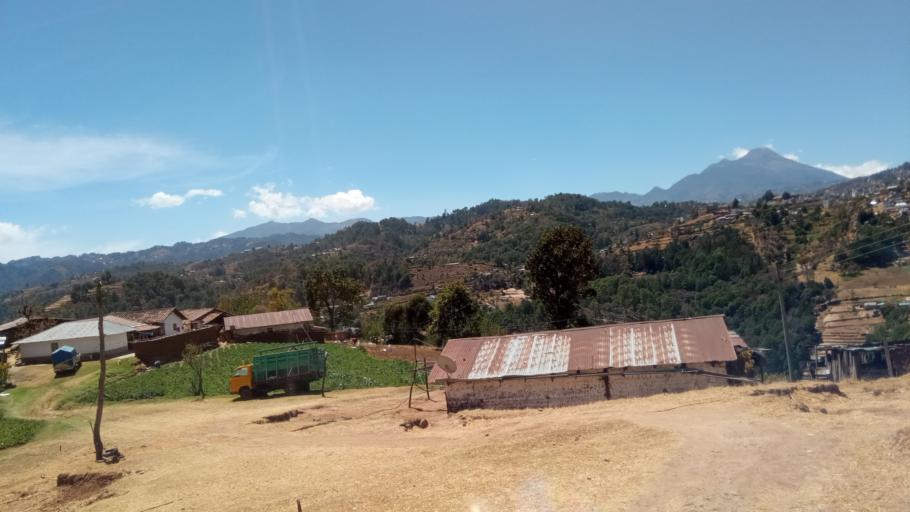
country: GT
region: San Marcos
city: Tejutla
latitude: 15.1295
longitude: -91.7930
